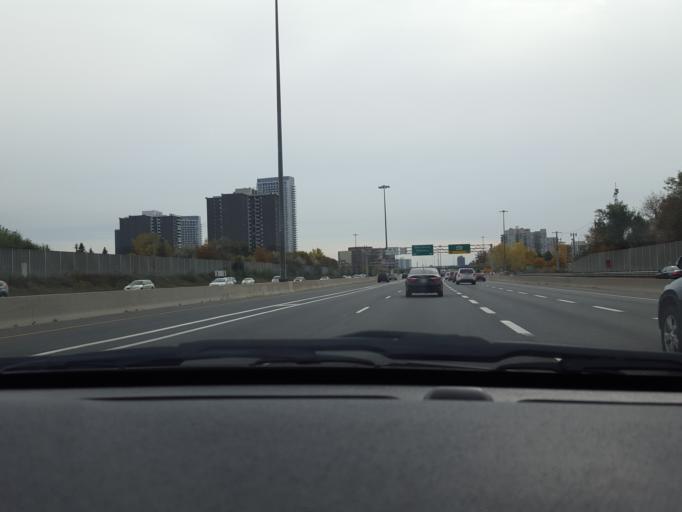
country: CA
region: Ontario
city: Willowdale
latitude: 43.7819
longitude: -79.3409
